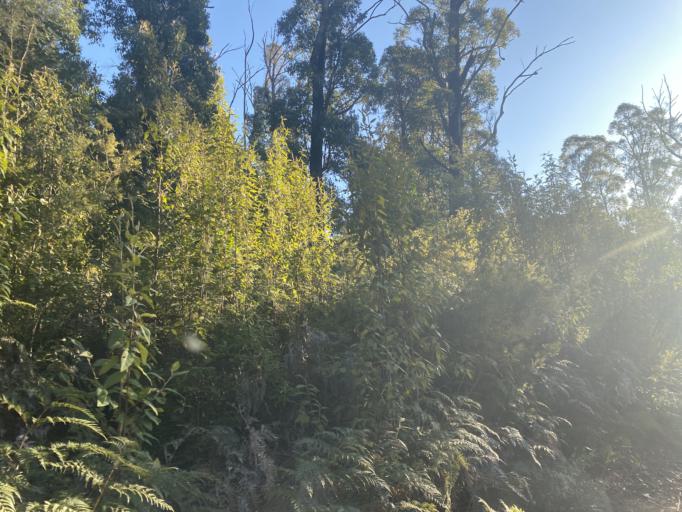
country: AU
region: Victoria
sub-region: Yarra Ranges
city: Healesville
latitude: -37.4782
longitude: 145.5960
